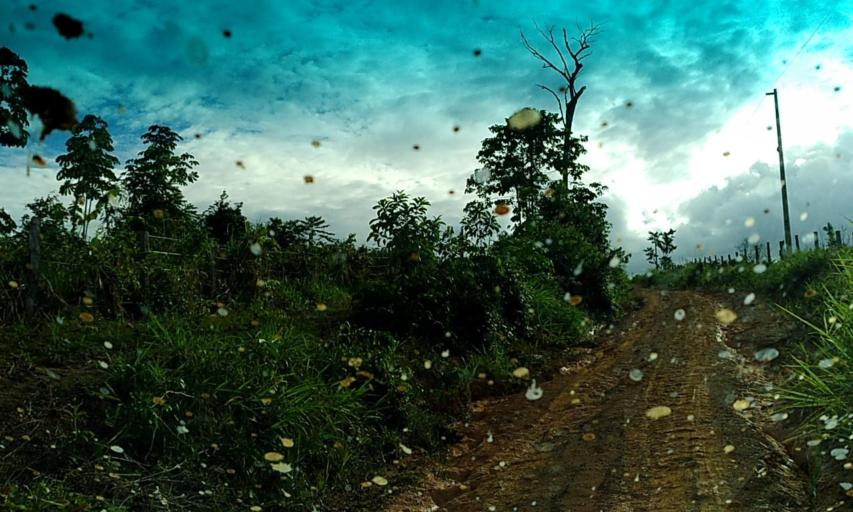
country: BR
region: Para
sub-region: Senador Jose Porfirio
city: Senador Jose Porfirio
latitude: -3.0058
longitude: -51.7429
